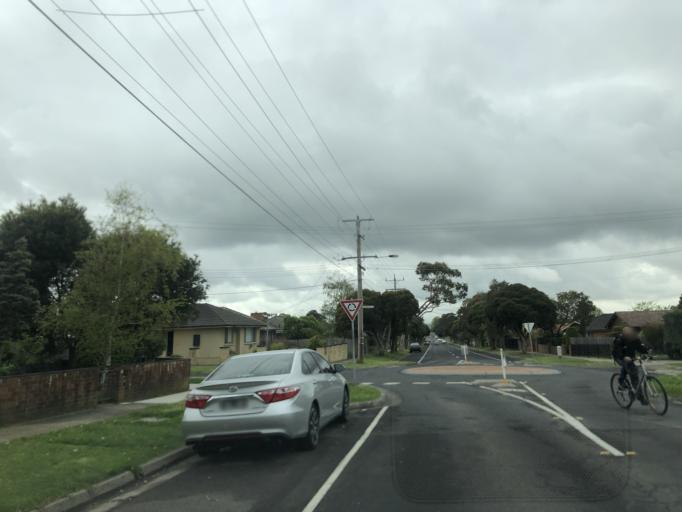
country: AU
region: Victoria
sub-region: Greater Dandenong
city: Dandenong North
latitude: -37.9598
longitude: 145.2115
